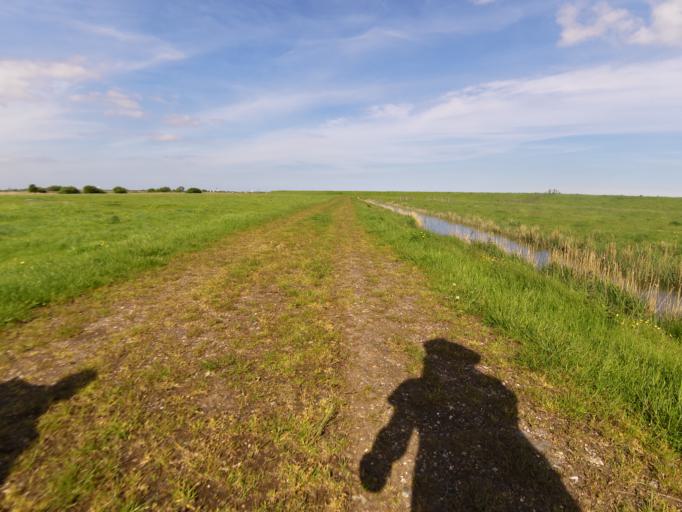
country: GB
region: England
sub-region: Norfolk
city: Great Yarmouth
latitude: 52.6156
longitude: 1.6905
